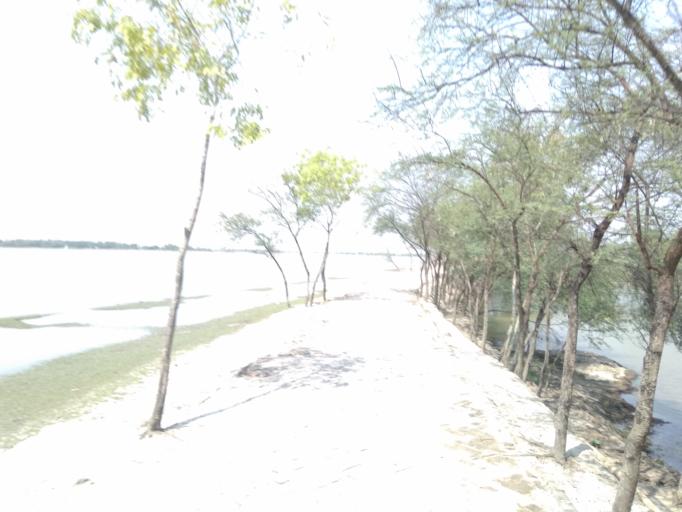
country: IN
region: West Bengal
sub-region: North 24 Parganas
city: Taki
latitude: 22.3949
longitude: 89.1916
